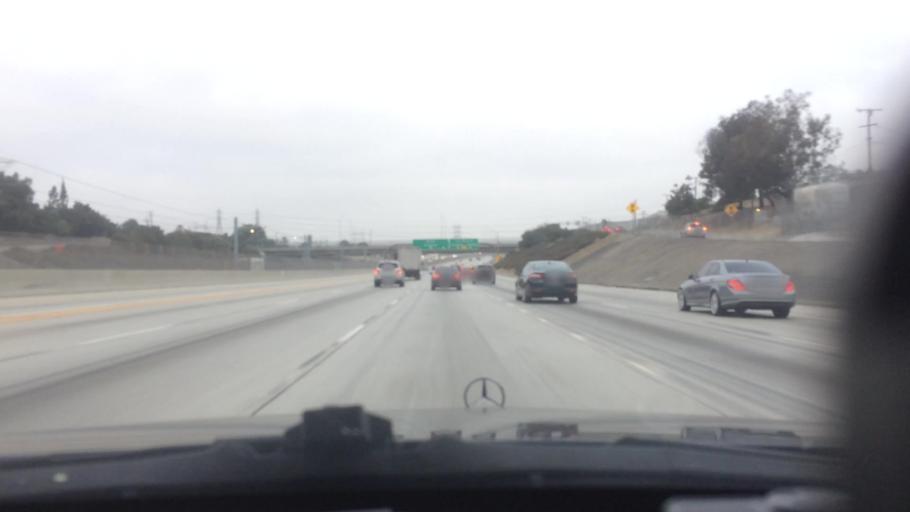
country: US
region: California
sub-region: Los Angeles County
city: Paramount
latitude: 33.9116
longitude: -118.1653
